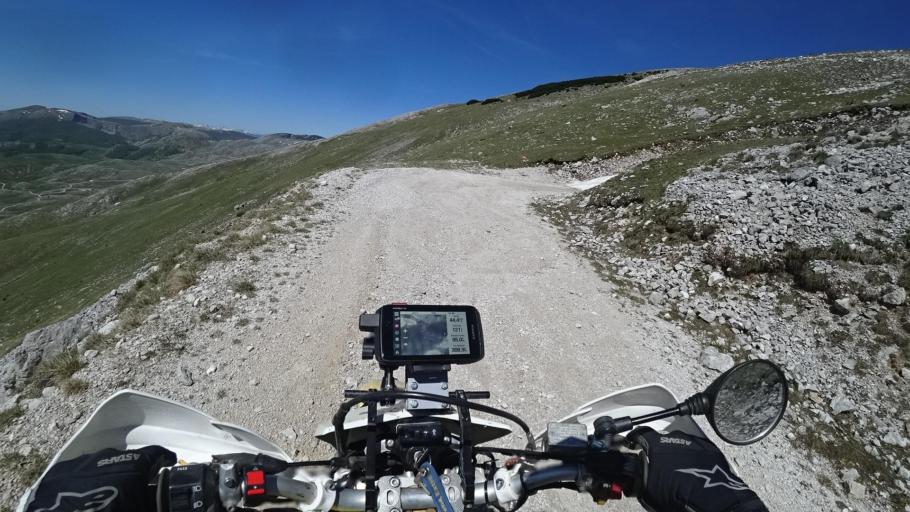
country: BA
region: Federation of Bosnia and Herzegovina
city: Gracanica
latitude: 43.6973
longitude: 18.2594
